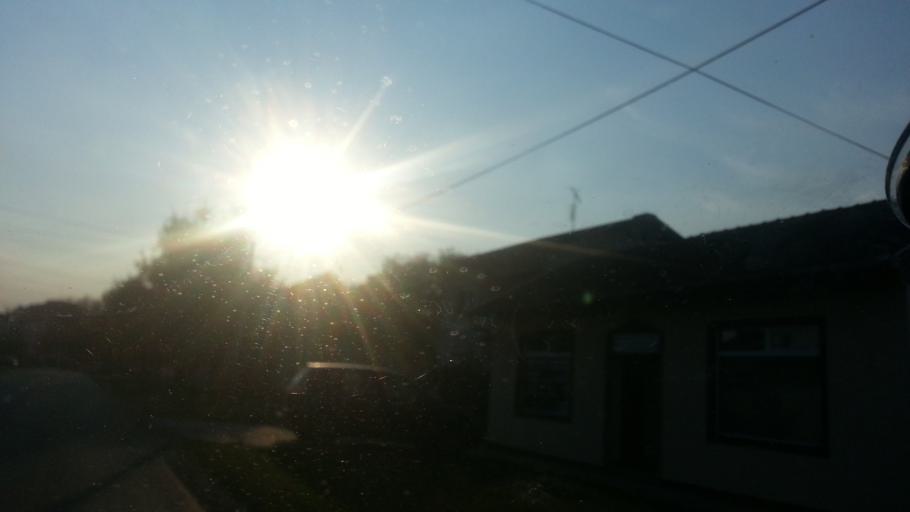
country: RS
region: Autonomna Pokrajina Vojvodina
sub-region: Sremski Okrug
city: Ingija
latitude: 45.0502
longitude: 20.0880
